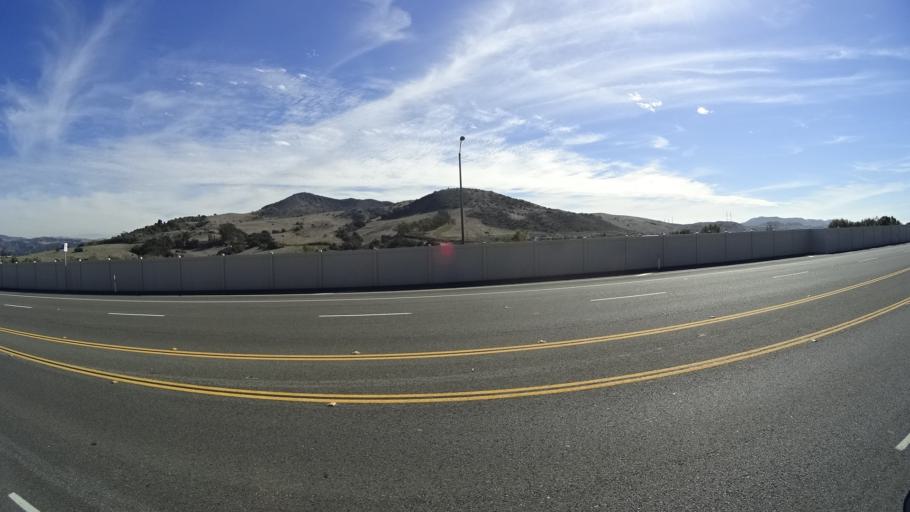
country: US
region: California
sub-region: Orange County
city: Ladera Ranch
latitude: 33.5269
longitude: -117.6157
